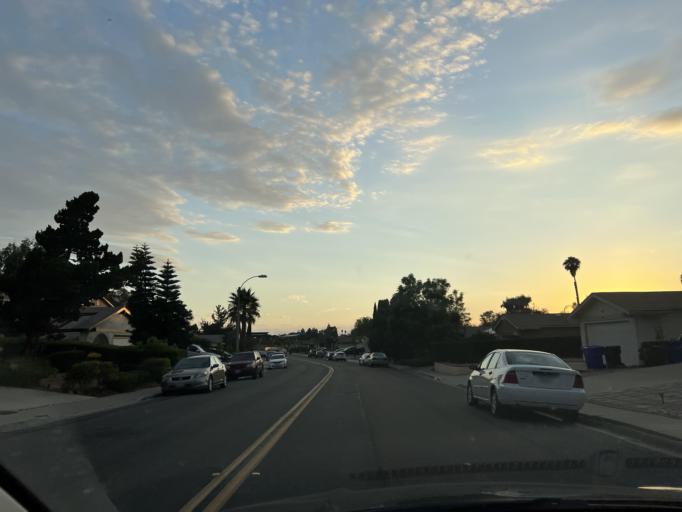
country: US
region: California
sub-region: San Diego County
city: Fairbanks Ranch
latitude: 32.9074
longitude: -117.1516
